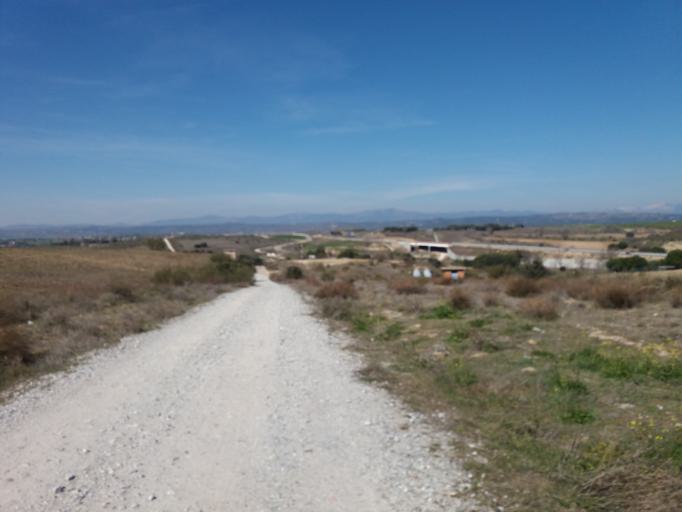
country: ES
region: Madrid
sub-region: Provincia de Madrid
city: Majadahonda
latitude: 40.4769
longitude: -3.9103
